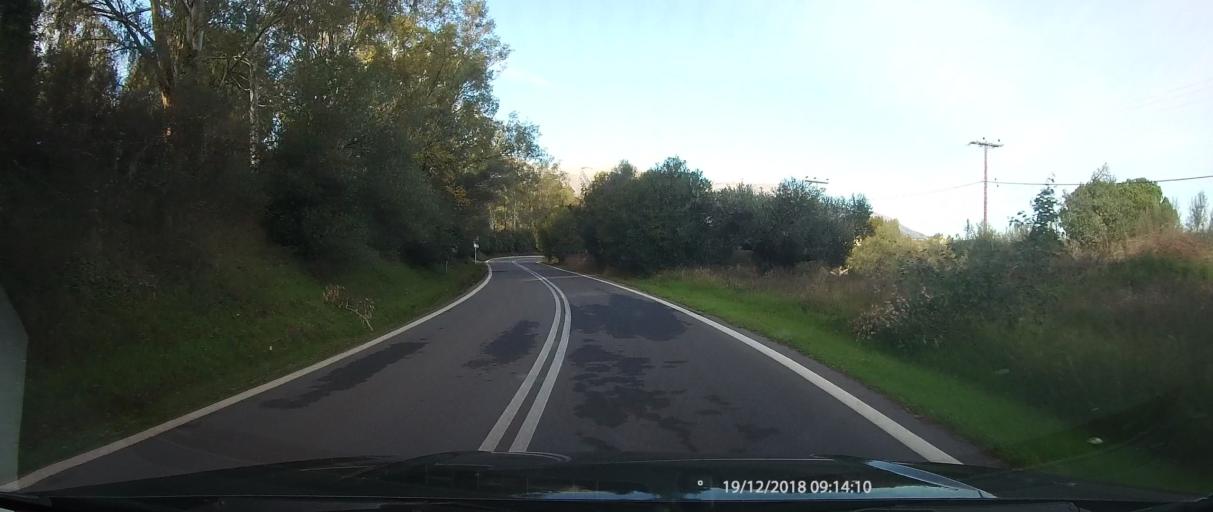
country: GR
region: Peloponnese
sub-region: Nomos Lakonias
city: Magoula
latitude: 37.0850
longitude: 22.3916
